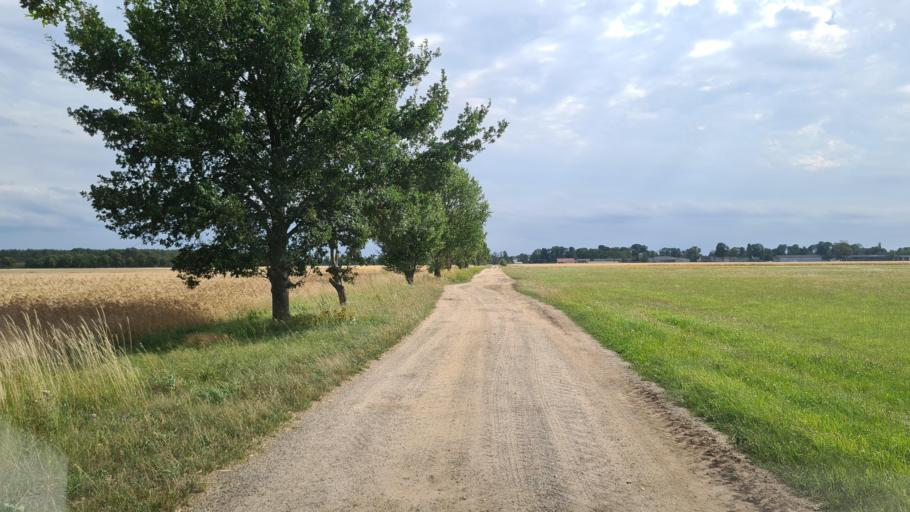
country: DE
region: Saxony-Anhalt
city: Holzdorf
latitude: 51.8069
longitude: 13.1815
